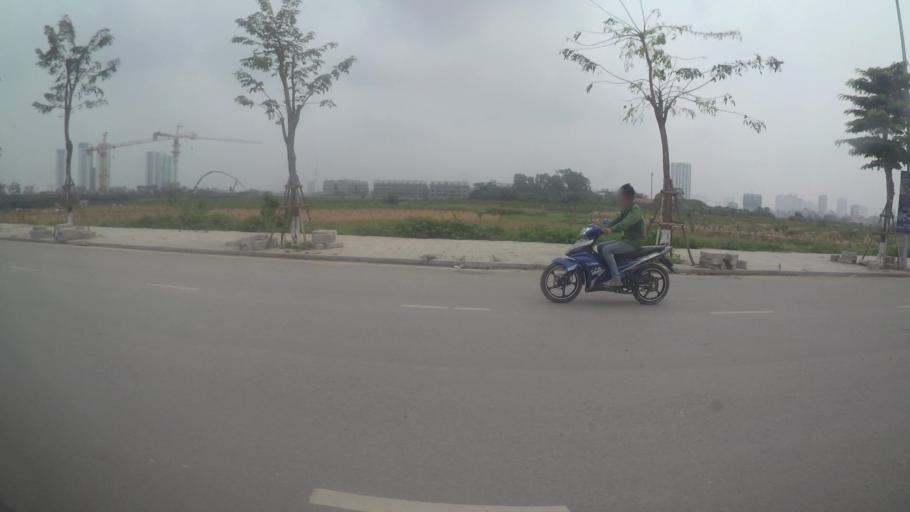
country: VN
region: Ha Noi
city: Ha Dong
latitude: 20.9824
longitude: 105.7580
